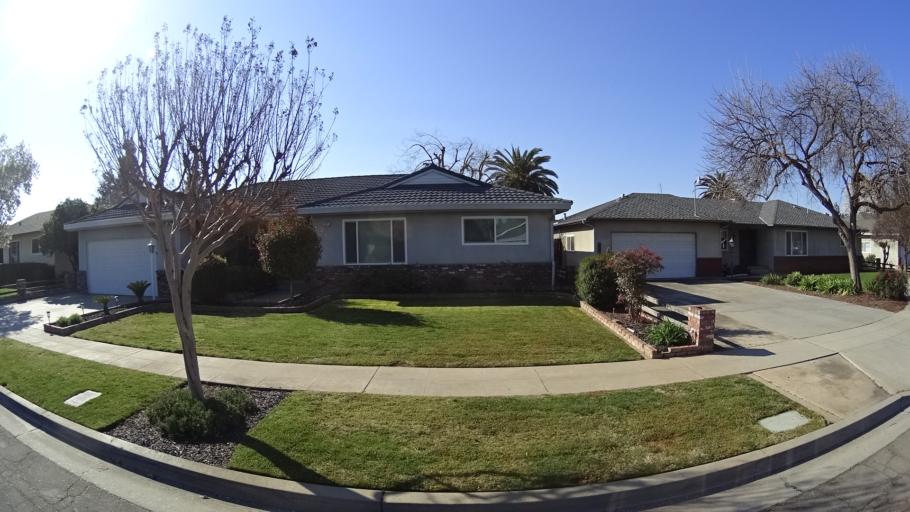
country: US
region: California
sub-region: Fresno County
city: Clovis
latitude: 36.8338
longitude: -119.7708
